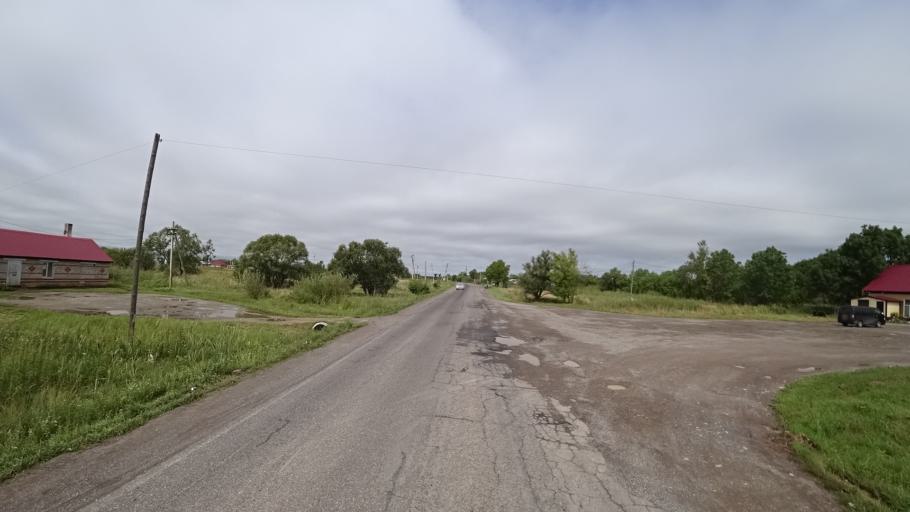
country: RU
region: Primorskiy
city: Monastyrishche
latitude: 44.1943
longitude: 132.4800
